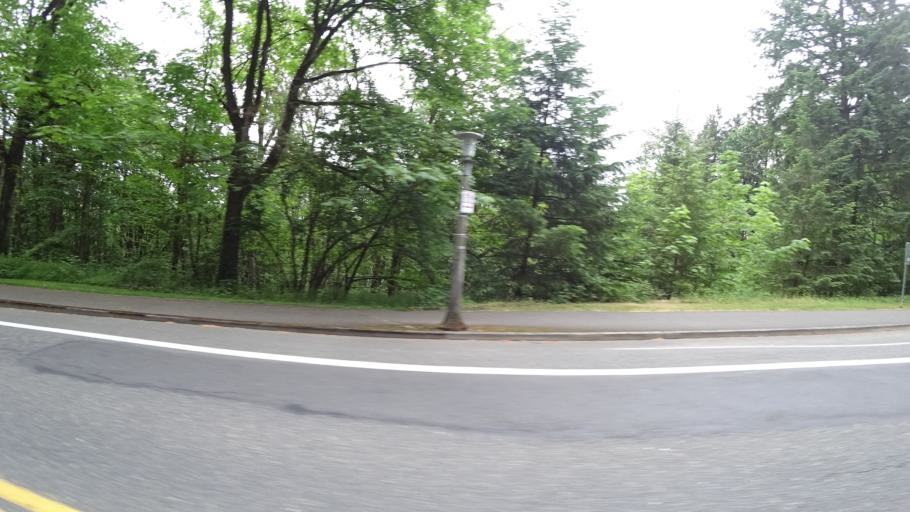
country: US
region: Oregon
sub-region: Multnomah County
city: Portland
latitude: 45.4881
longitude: -122.6852
